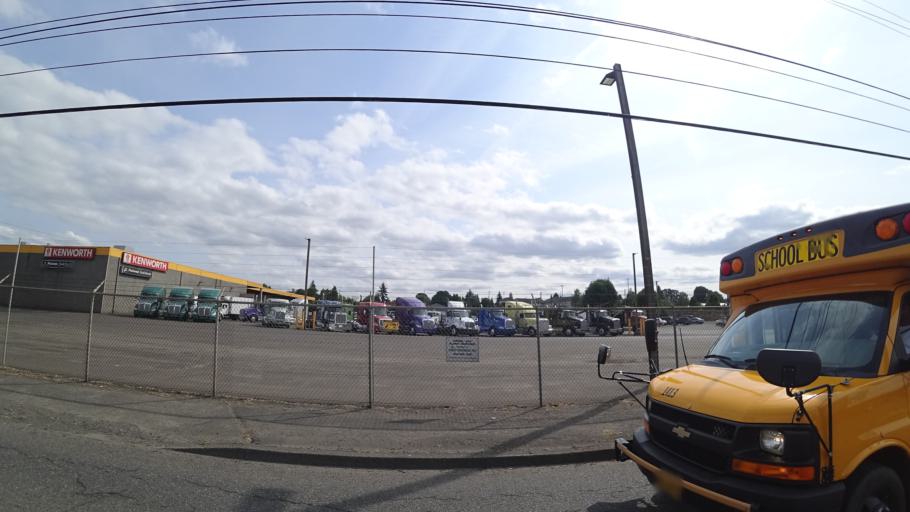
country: US
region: Washington
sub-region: Clark County
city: Vancouver
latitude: 45.5807
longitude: -122.6598
